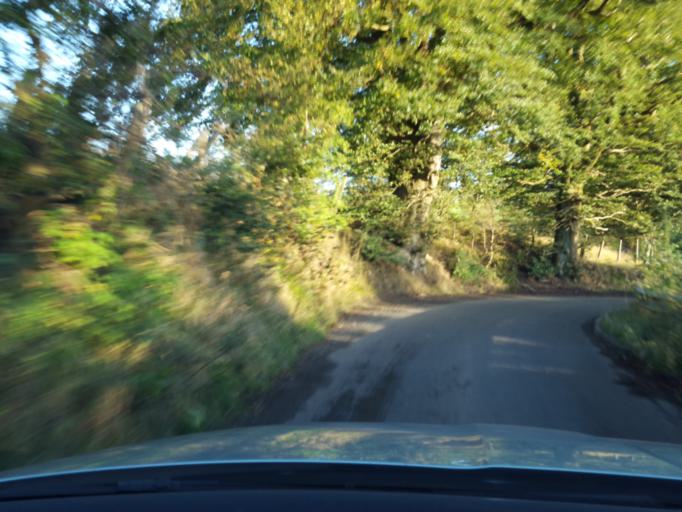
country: GB
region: Scotland
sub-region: North Lanarkshire
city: Cumbernauld
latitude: 55.9298
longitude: -3.9453
